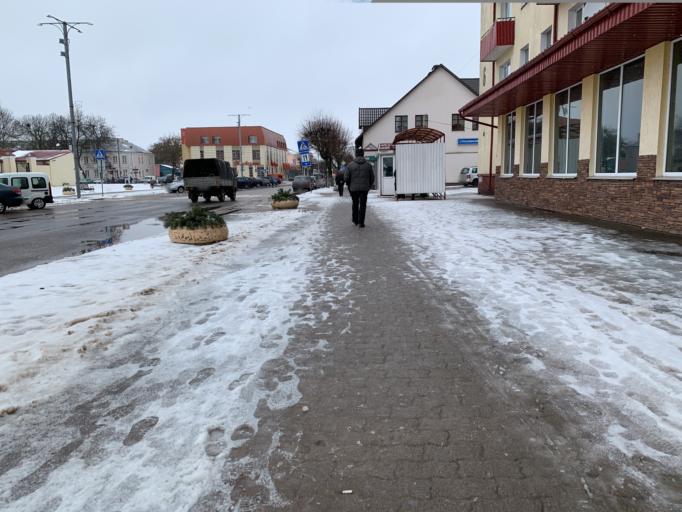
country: BY
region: Minsk
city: Nyasvizh
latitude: 53.2193
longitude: 26.6825
